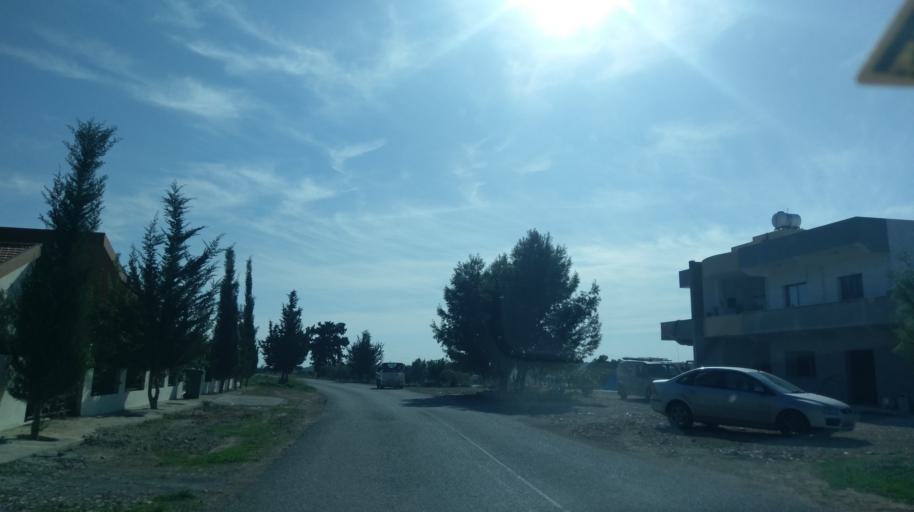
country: CY
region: Ammochostos
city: Trikomo
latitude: 35.3275
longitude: 33.9324
